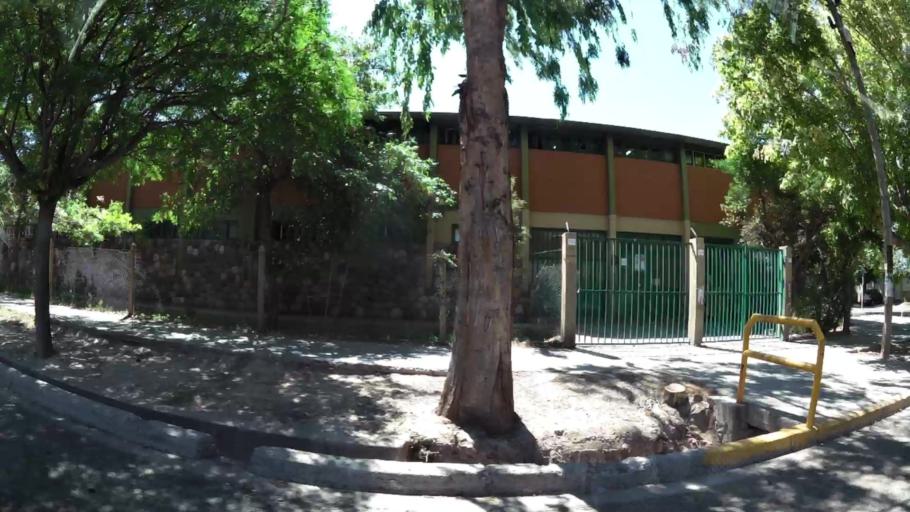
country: AR
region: Mendoza
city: Las Heras
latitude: -32.8484
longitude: -68.8470
